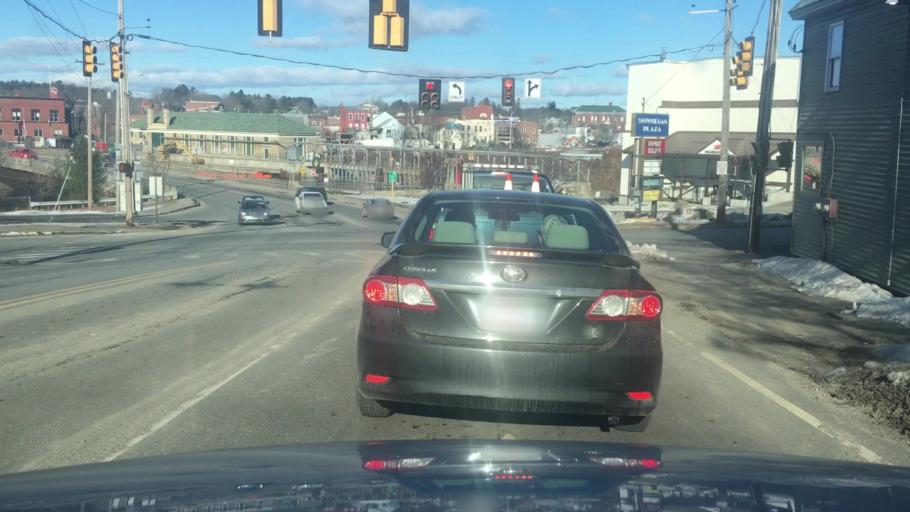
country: US
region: Maine
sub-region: Somerset County
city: Skowhegan
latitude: 44.7622
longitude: -69.7170
